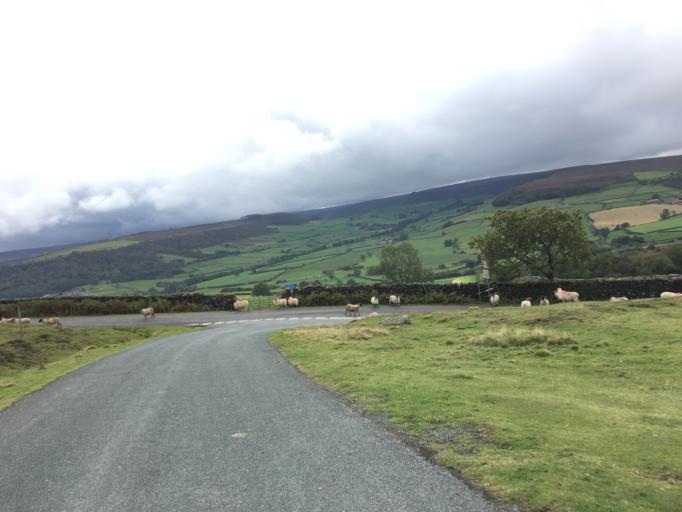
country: GB
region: England
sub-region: North Yorkshire
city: Danby
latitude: 54.4672
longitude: -0.8830
